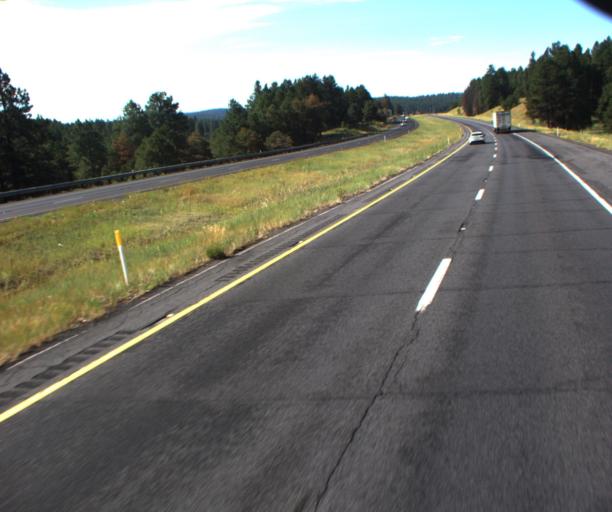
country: US
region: Arizona
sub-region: Coconino County
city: Kachina Village
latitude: 35.1128
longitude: -111.6816
